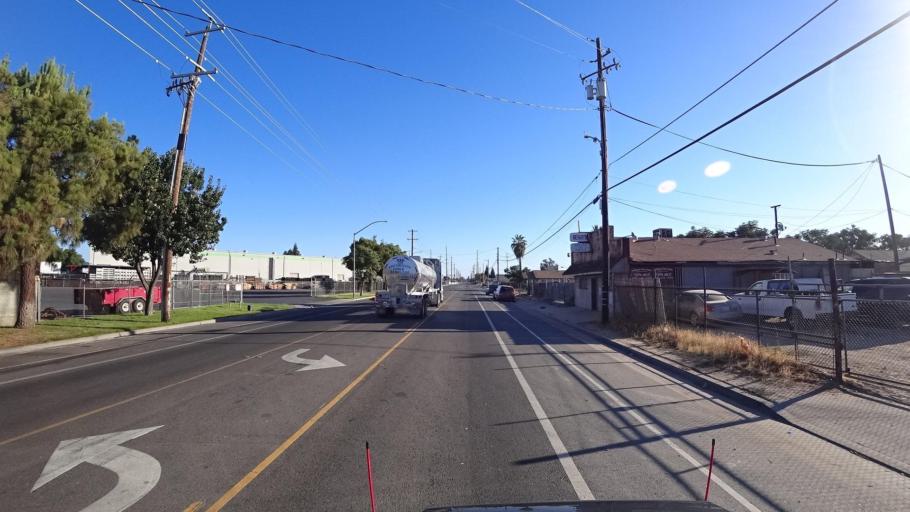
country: US
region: California
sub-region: Fresno County
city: Fresno
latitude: 36.7118
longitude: -119.7637
